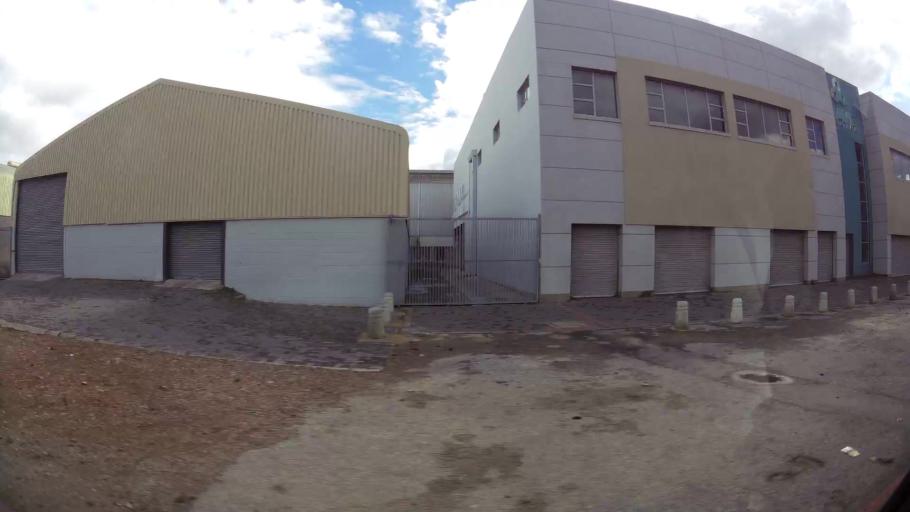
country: ZA
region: Eastern Cape
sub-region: Nelson Mandela Bay Metropolitan Municipality
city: Port Elizabeth
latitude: -33.9264
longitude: 25.5671
